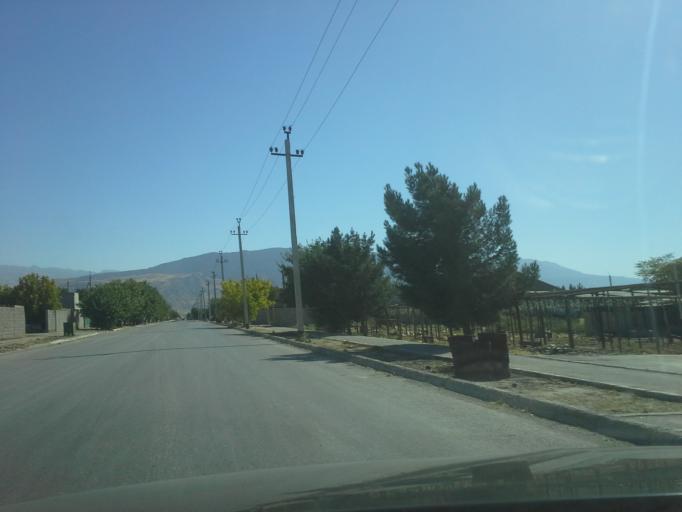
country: TM
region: Ahal
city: Abadan
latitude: 38.0827
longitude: 58.1590
